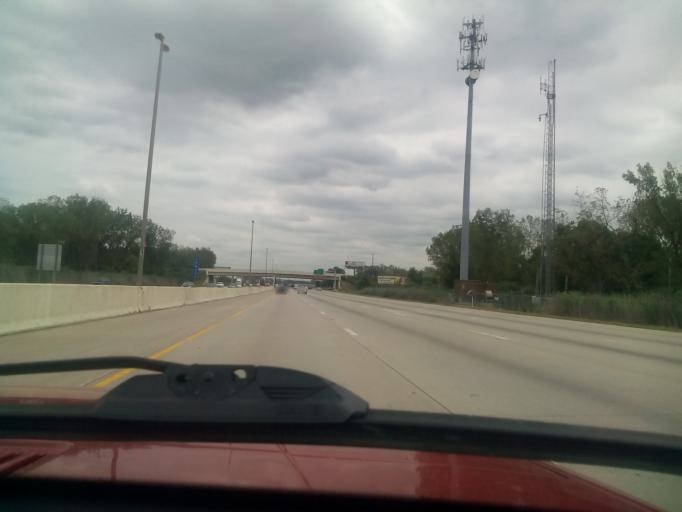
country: US
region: Indiana
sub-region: Lake County
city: Gary
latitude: 41.5697
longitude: -87.3798
